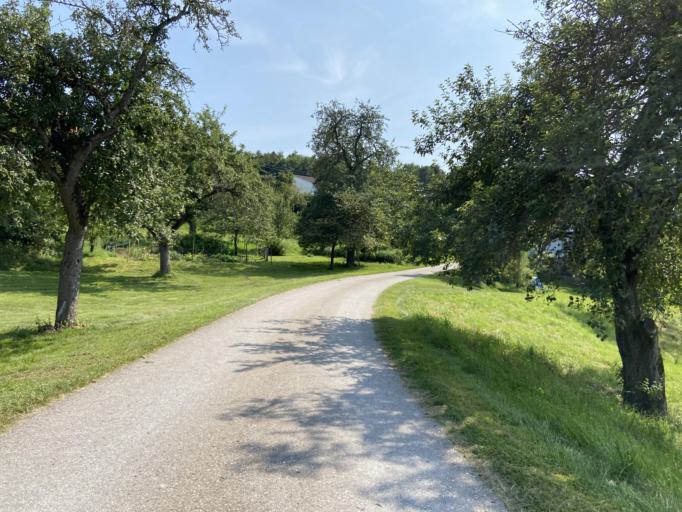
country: DE
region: Baden-Wuerttemberg
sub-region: Tuebingen Region
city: Bingen
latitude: 48.1074
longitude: 9.2922
